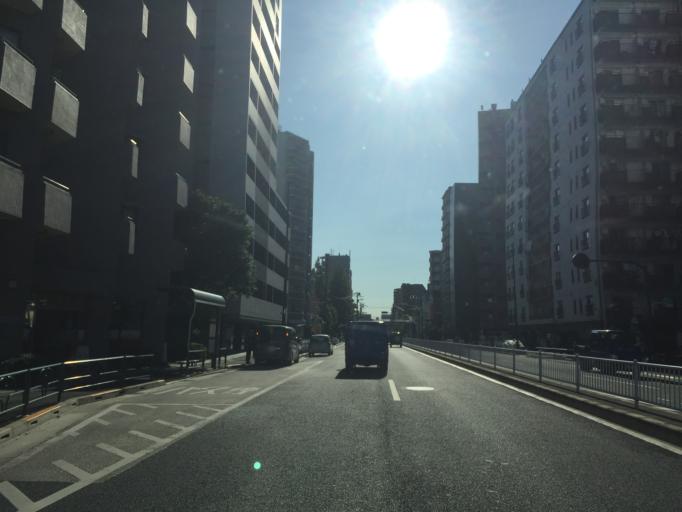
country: JP
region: Saitama
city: Kawaguchi
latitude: 35.7544
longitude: 139.7435
